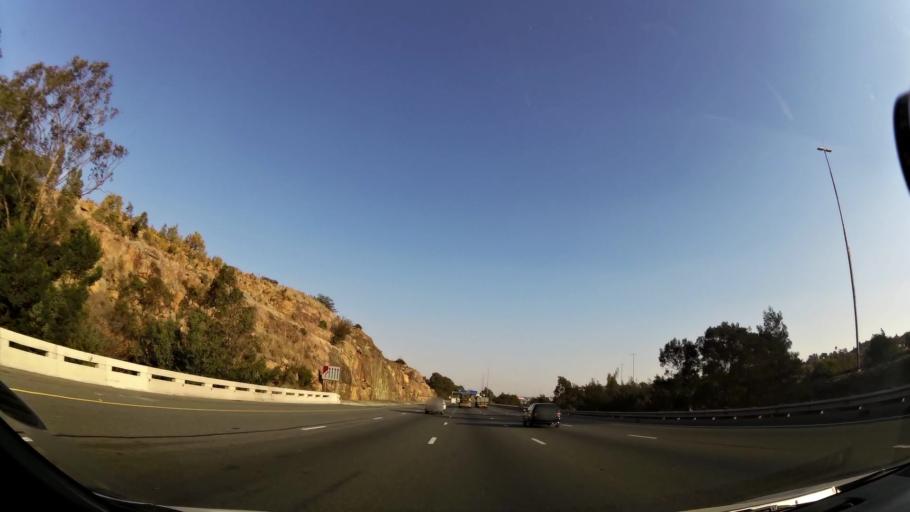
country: ZA
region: Gauteng
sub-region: Ekurhuleni Metropolitan Municipality
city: Germiston
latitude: -26.2490
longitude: 28.1230
